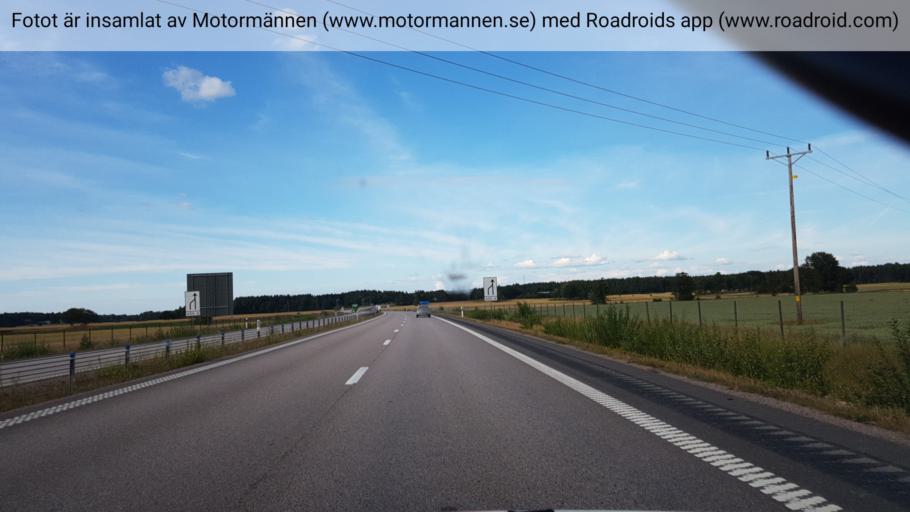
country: SE
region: Vaestra Goetaland
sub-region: Gotene Kommun
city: Goetene
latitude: 58.5467
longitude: 13.5452
